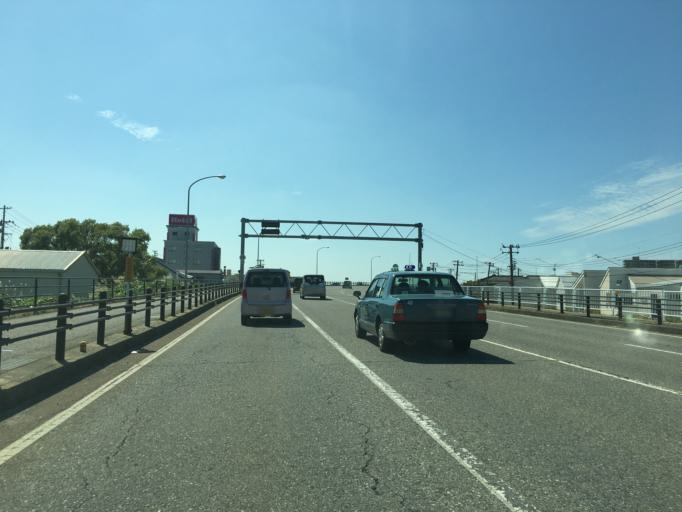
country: JP
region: Niigata
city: Niigata-shi
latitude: 37.8995
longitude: 139.0132
